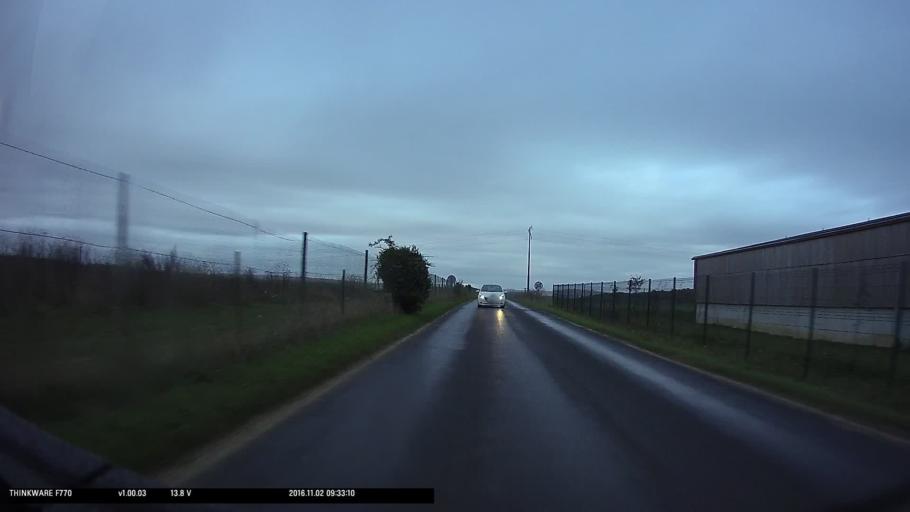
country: FR
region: Ile-de-France
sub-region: Departement du Val-d'Oise
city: Courdimanche
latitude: 49.0630
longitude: 2.0022
